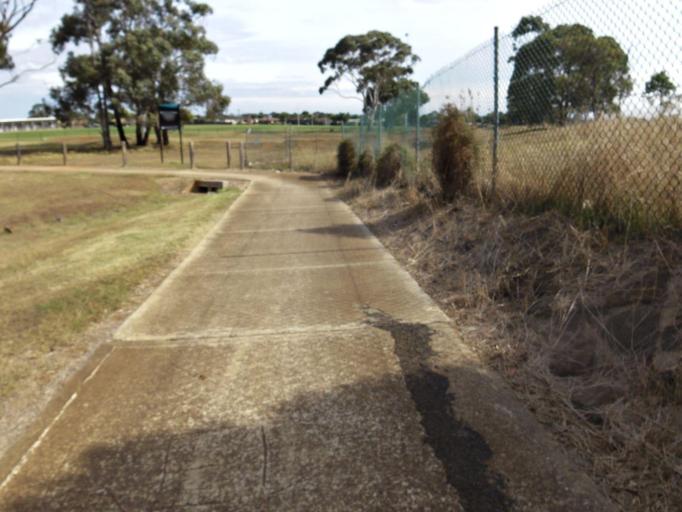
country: AU
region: Victoria
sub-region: Melton
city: Melton West
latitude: -37.6914
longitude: 144.5730
